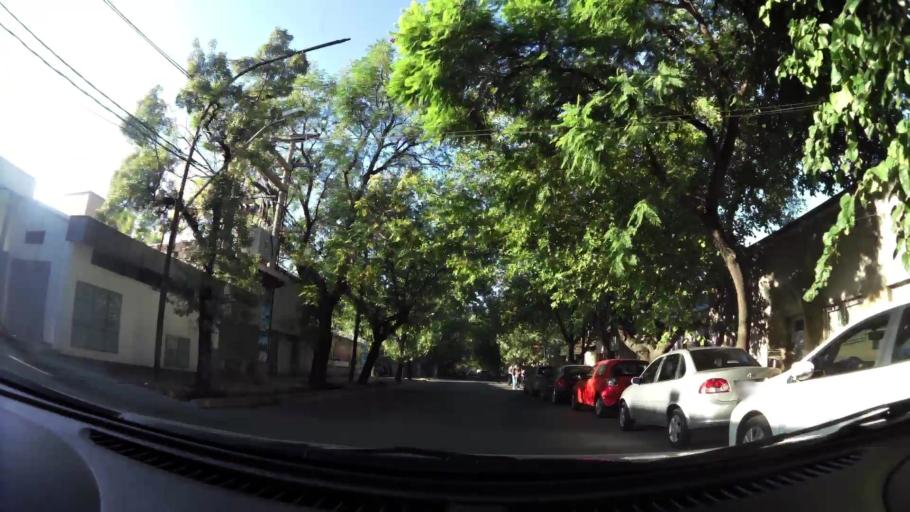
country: AR
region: Mendoza
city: Las Heras
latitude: -32.8706
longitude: -68.8292
